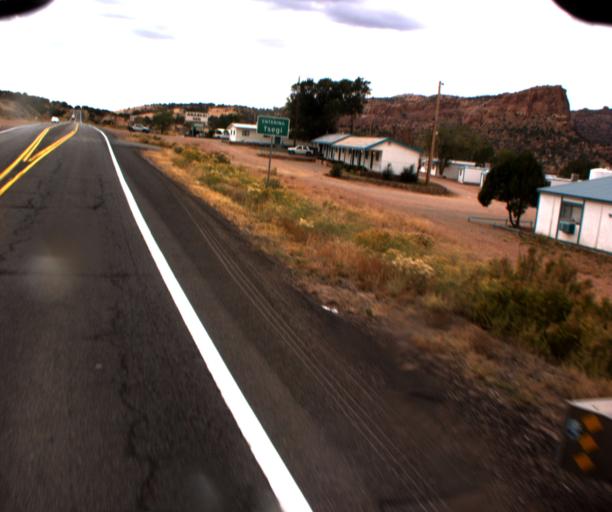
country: US
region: Arizona
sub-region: Navajo County
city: Kayenta
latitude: 36.6512
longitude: -110.4276
